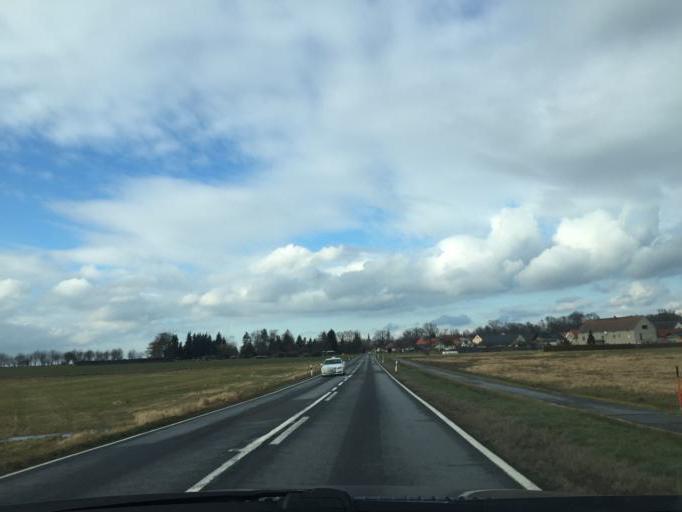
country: DE
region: Saxony
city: Wachau
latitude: 51.1544
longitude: 13.8902
